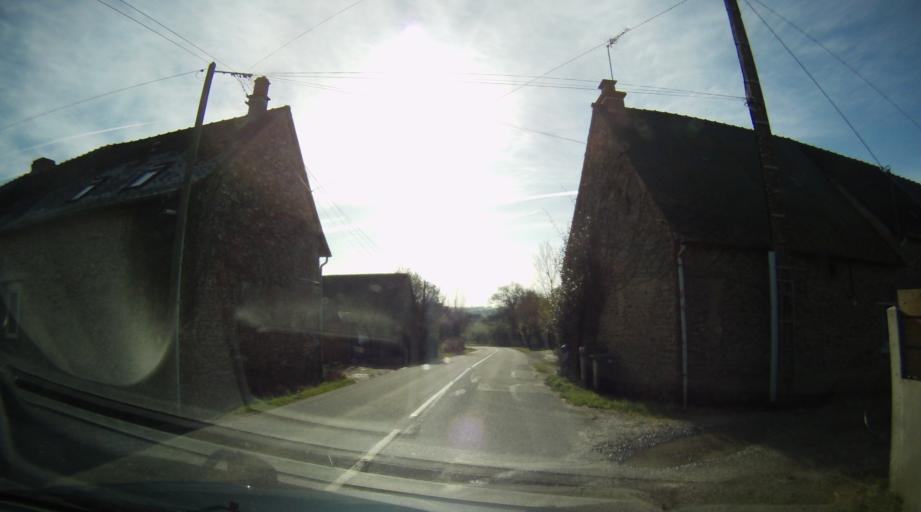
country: FR
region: Brittany
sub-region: Departement d'Ille-et-Vilaine
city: Chanteloup
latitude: 47.9495
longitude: -1.6115
